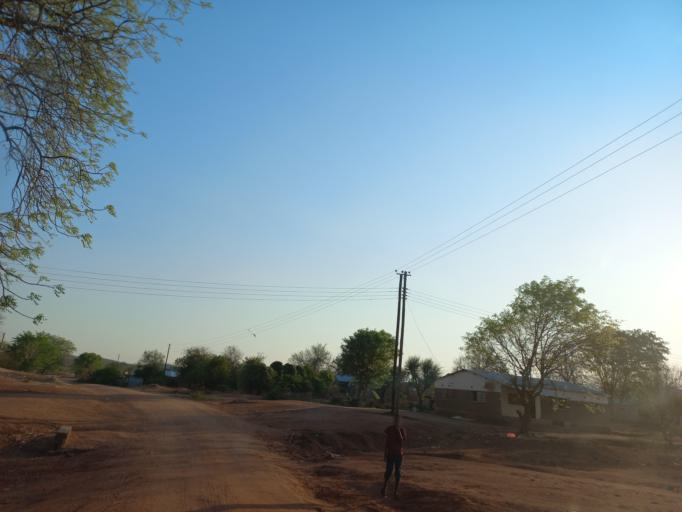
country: ZM
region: Lusaka
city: Luangwa
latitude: -15.6163
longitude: 30.3904
